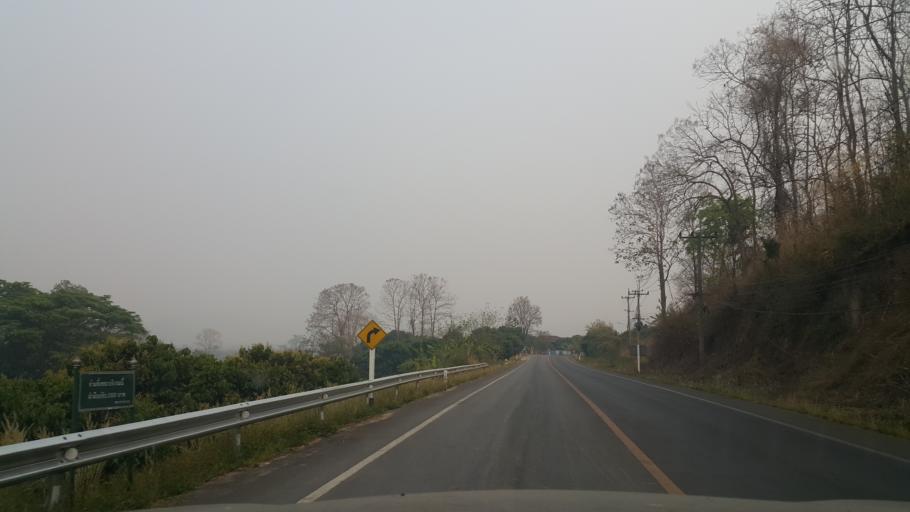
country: TH
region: Lamphun
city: Mae Tha
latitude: 18.5373
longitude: 99.2323
